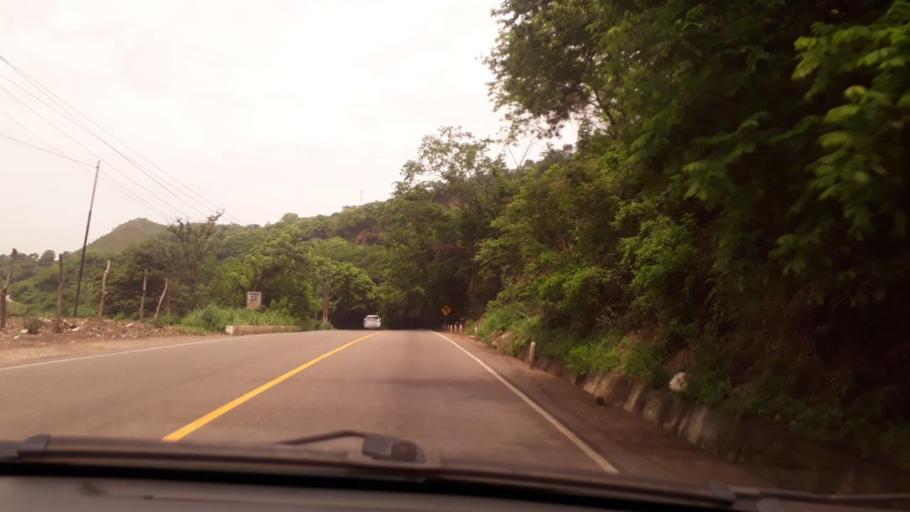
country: GT
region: Chiquimula
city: San Jacinto
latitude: 14.7044
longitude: -89.4983
